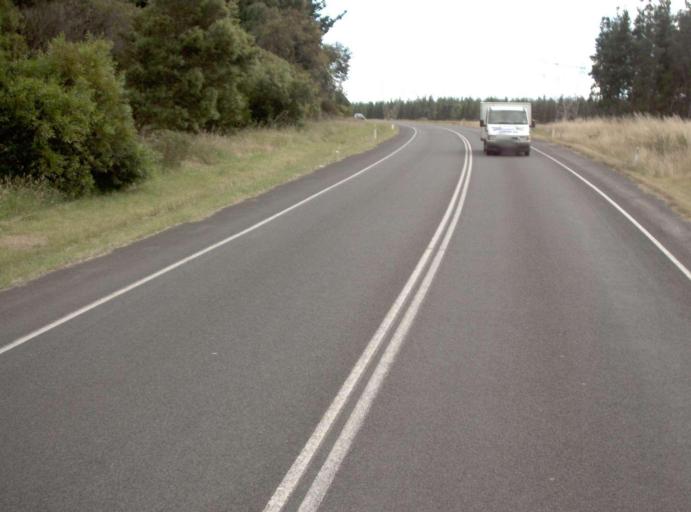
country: AU
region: Victoria
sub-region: Latrobe
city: Morwell
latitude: -38.1967
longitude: 146.4483
